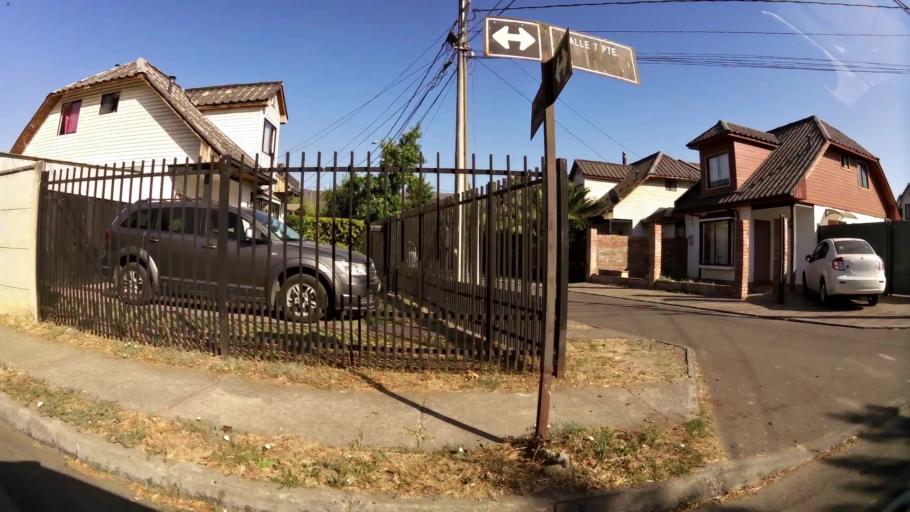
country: CL
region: Maule
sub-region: Provincia de Talca
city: Talca
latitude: -35.4150
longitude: -71.6717
